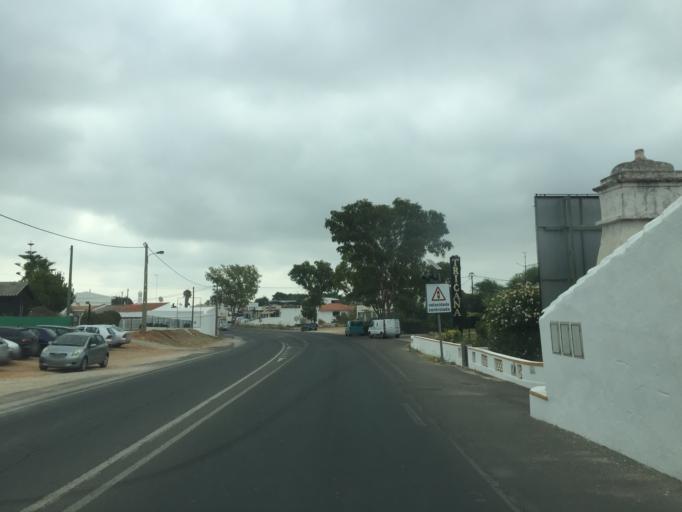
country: PT
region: Faro
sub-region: Faro
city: Santa Barbara de Nexe
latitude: 37.0774
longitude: -7.9893
